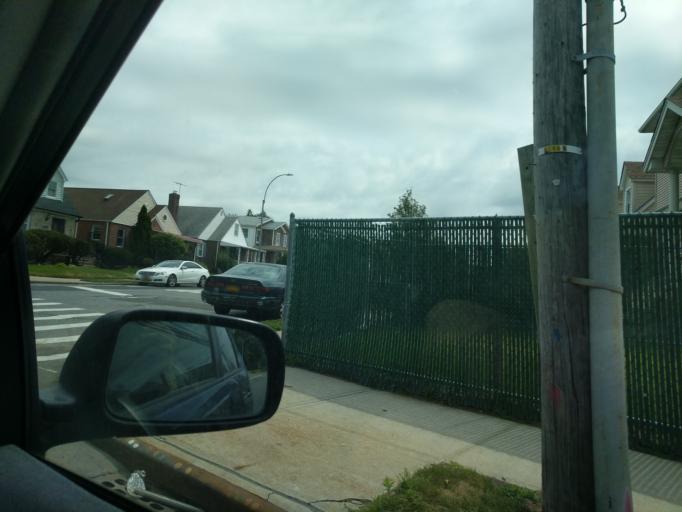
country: US
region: New York
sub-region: Nassau County
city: South Valley Stream
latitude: 40.6778
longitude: -73.7298
